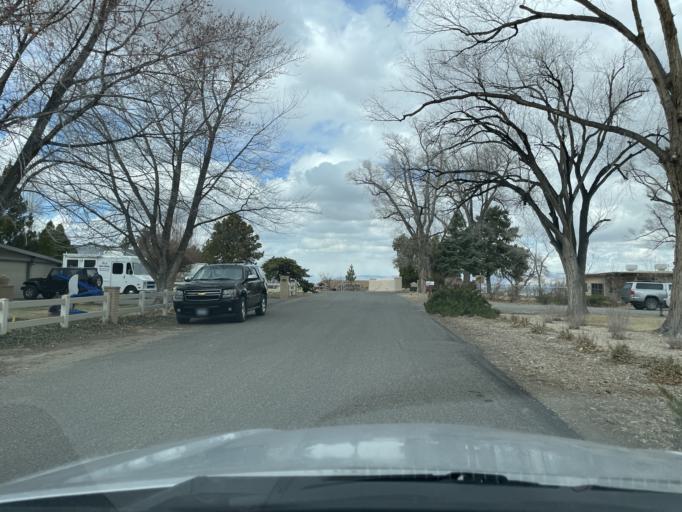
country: US
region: Colorado
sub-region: Mesa County
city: Redlands
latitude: 39.0615
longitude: -108.5977
